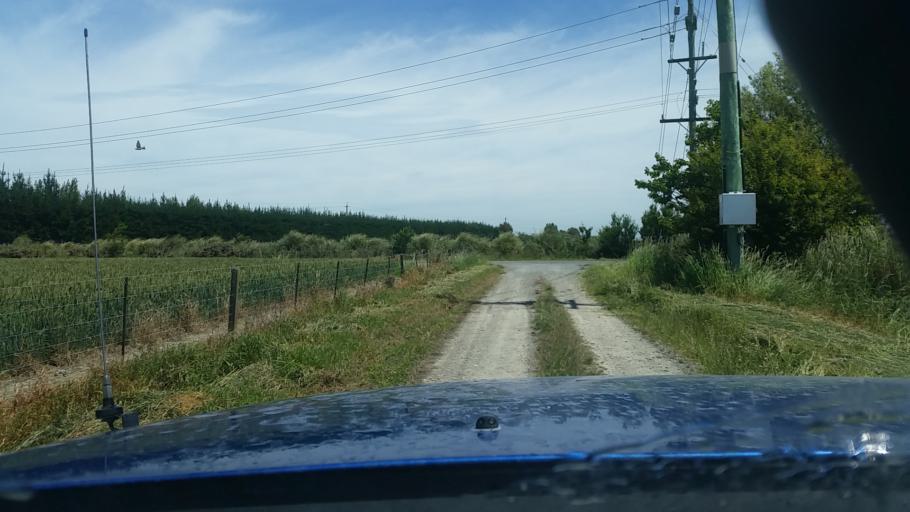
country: NZ
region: Canterbury
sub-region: Ashburton District
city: Tinwald
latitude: -44.0060
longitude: 171.7708
